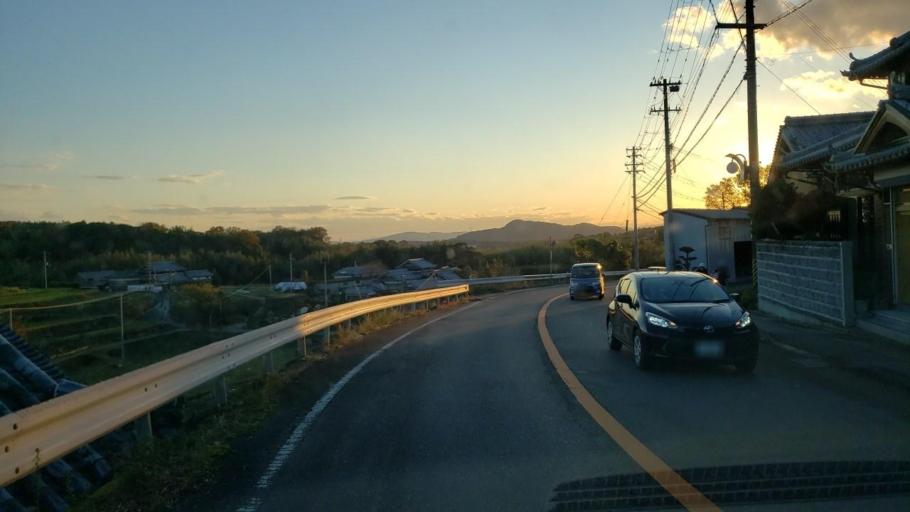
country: JP
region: Hyogo
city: Sumoto
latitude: 34.3861
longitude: 134.8080
